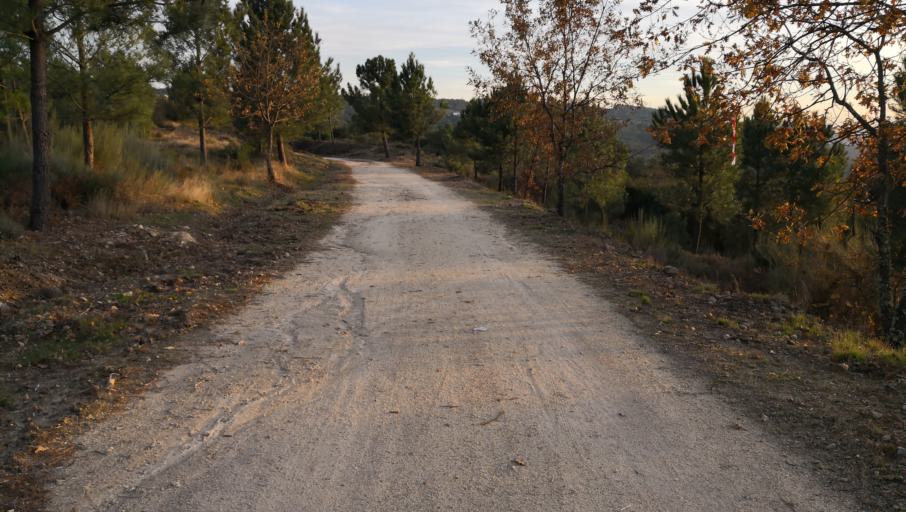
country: PT
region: Vila Real
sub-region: Vila Real
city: Vila Real
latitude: 41.3354
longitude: -7.7096
